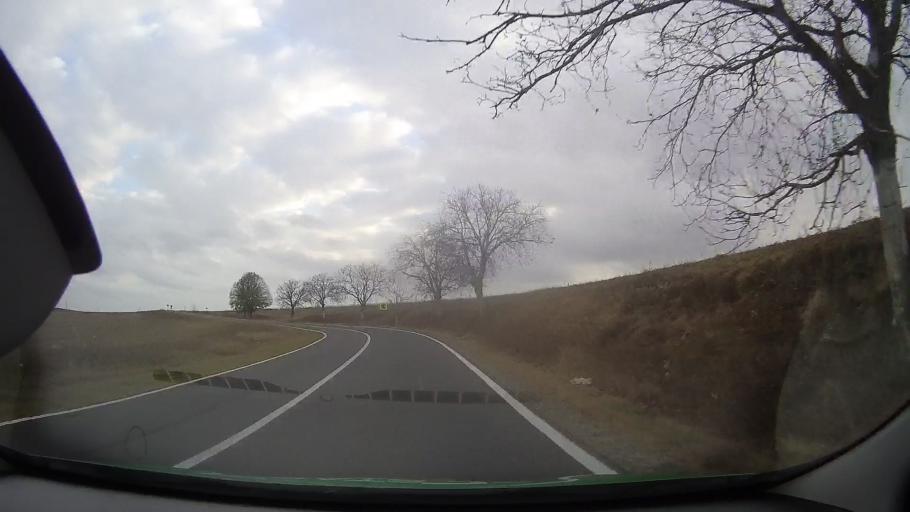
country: RO
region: Constanta
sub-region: Comuna Deleni
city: Deleni
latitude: 44.0957
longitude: 28.0166
